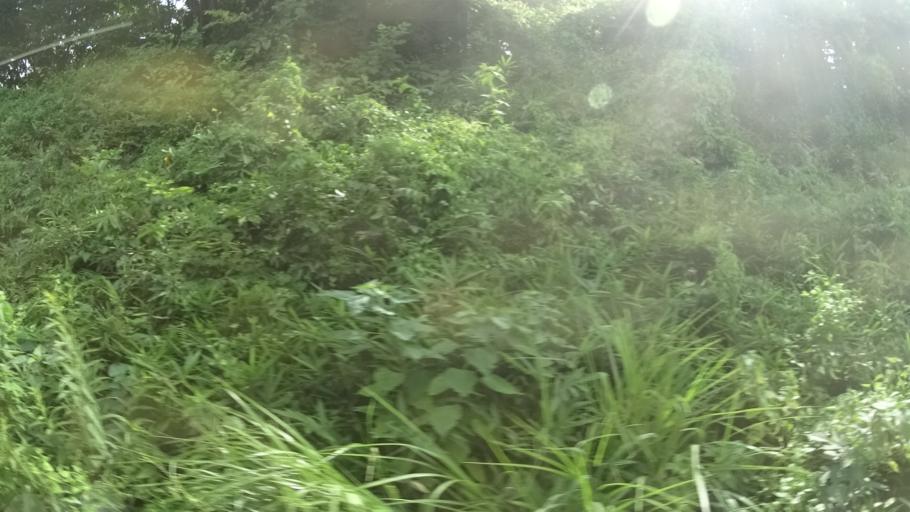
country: JP
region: Tochigi
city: Kanuma
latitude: 36.5741
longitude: 139.7614
